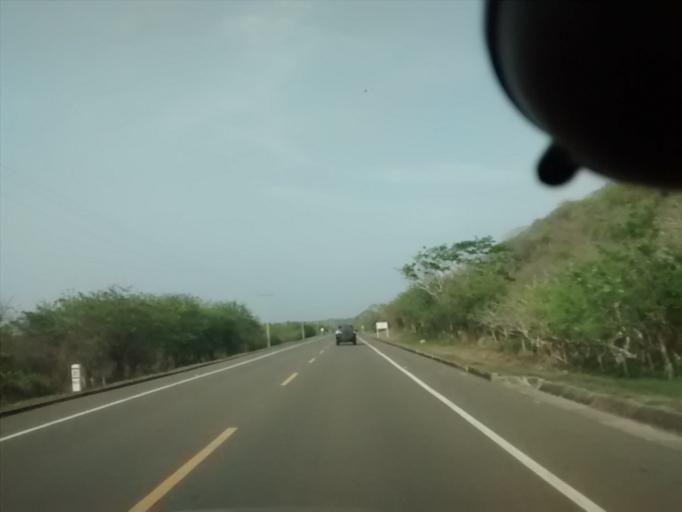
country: CO
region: Bolivar
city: Clemencia
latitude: 10.6272
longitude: -75.4321
